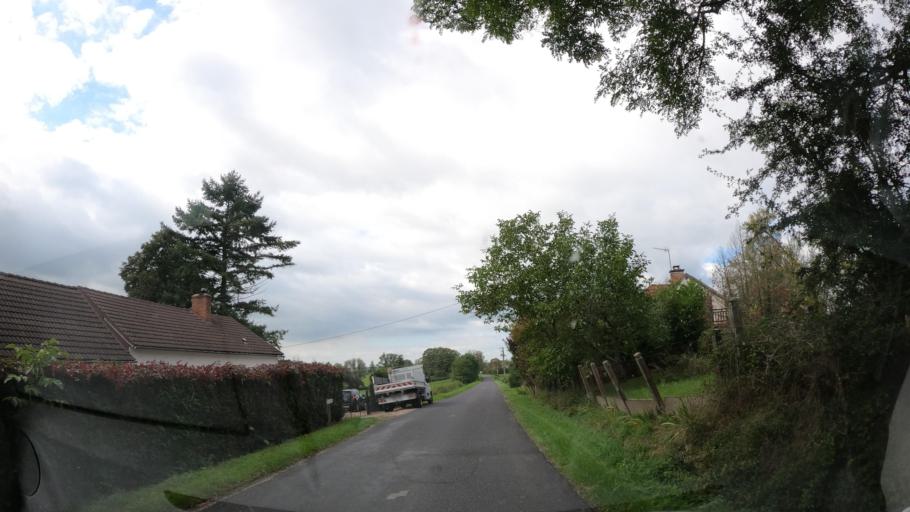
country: FR
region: Auvergne
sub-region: Departement de l'Allier
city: Lapalisse
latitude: 46.3467
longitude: 3.6303
